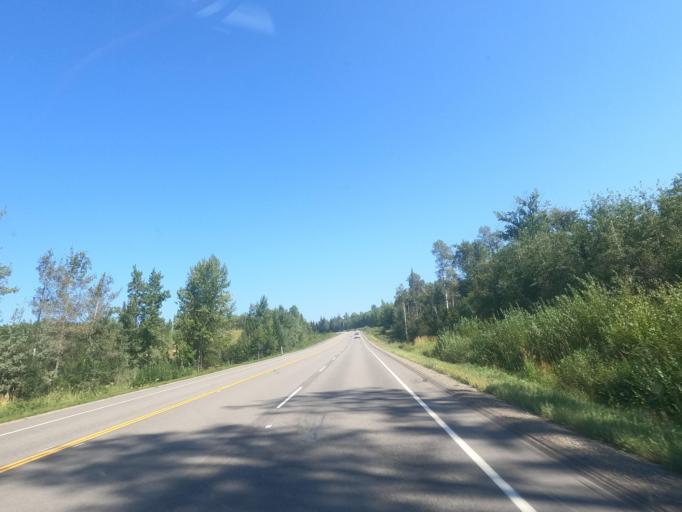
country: CA
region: British Columbia
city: Prince George
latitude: 53.9272
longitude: -122.5910
